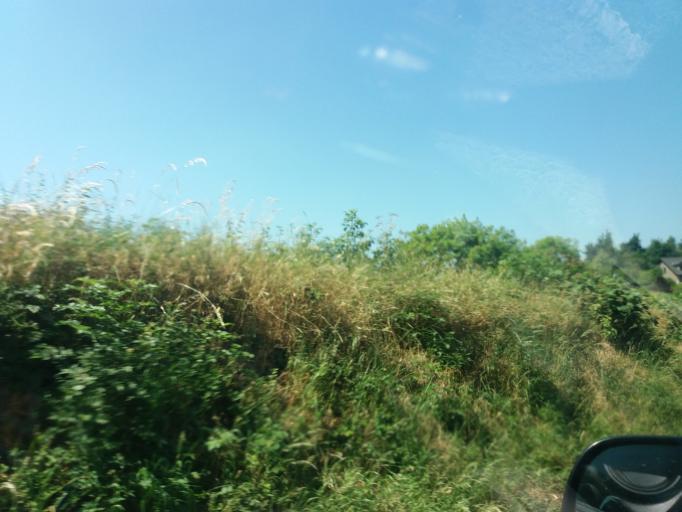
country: IE
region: Leinster
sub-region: An Mhi
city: Ashbourne
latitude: 53.5293
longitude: -6.3243
